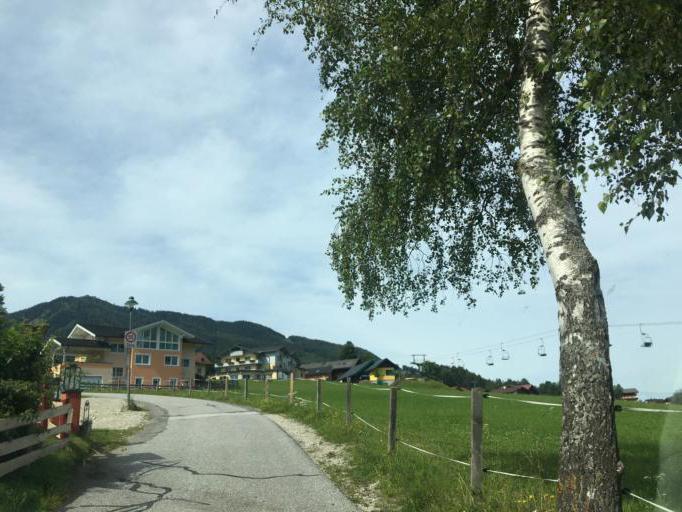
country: AT
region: Styria
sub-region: Politischer Bezirk Liezen
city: Schladming
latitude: 47.3847
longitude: 13.6702
